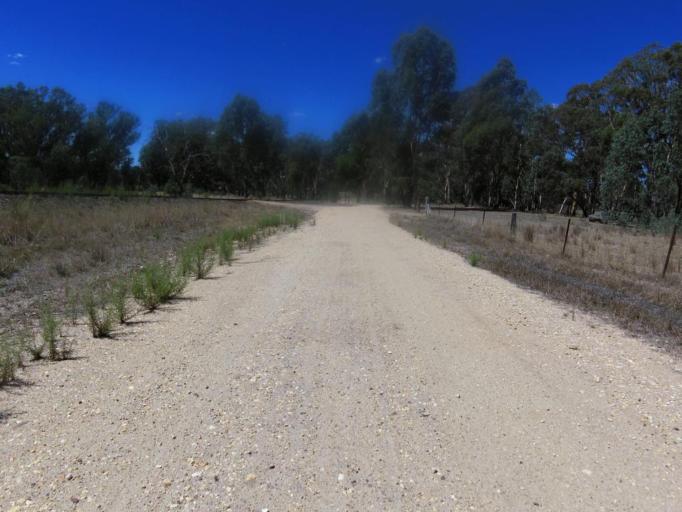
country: AU
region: Victoria
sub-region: Mount Alexander
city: Castlemaine
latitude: -37.0159
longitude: 144.1387
